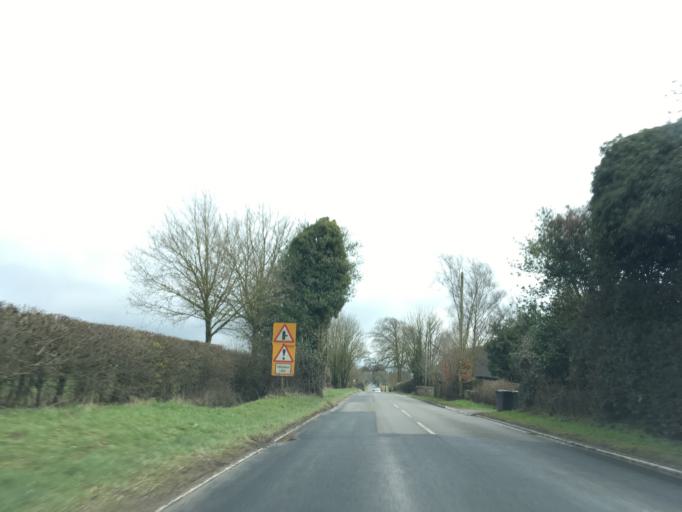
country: GB
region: England
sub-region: West Berkshire
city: Lambourn
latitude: 51.4769
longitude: -1.5306
